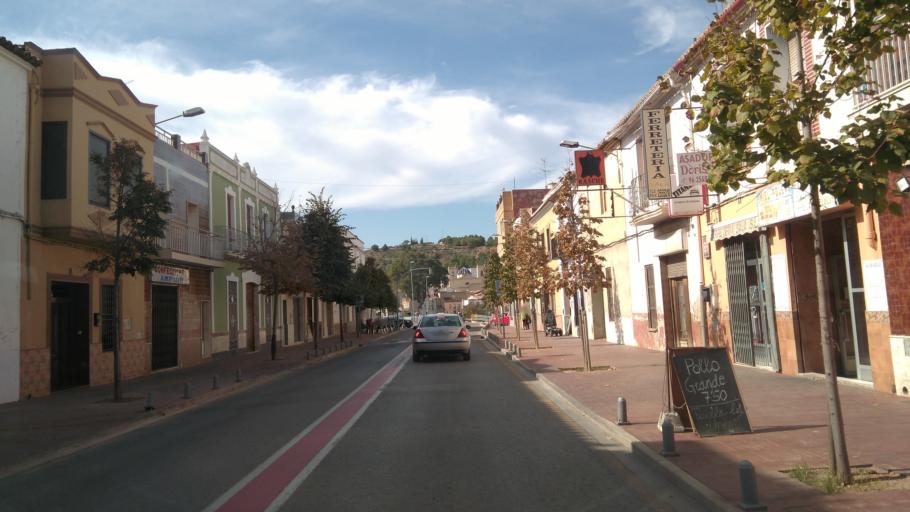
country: ES
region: Valencia
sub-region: Provincia de Valencia
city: Montroy
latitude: 39.3368
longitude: -0.6098
